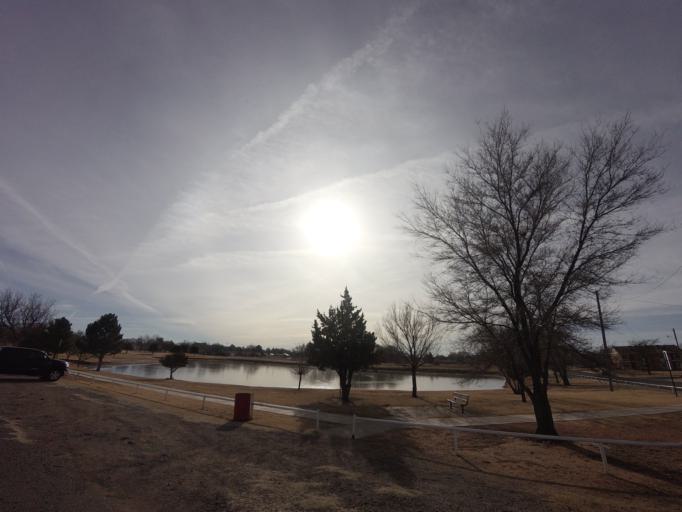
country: US
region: New Mexico
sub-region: Curry County
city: Clovis
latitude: 34.4135
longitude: -103.2203
